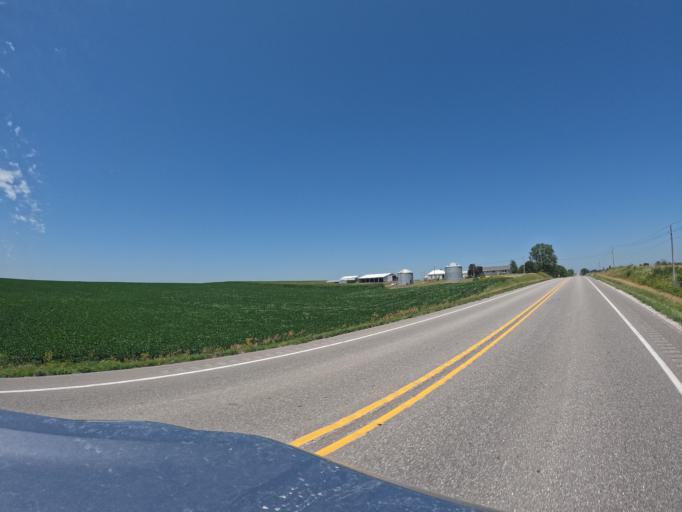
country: US
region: Iowa
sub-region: Keokuk County
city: Sigourney
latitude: 41.4575
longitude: -92.3551
